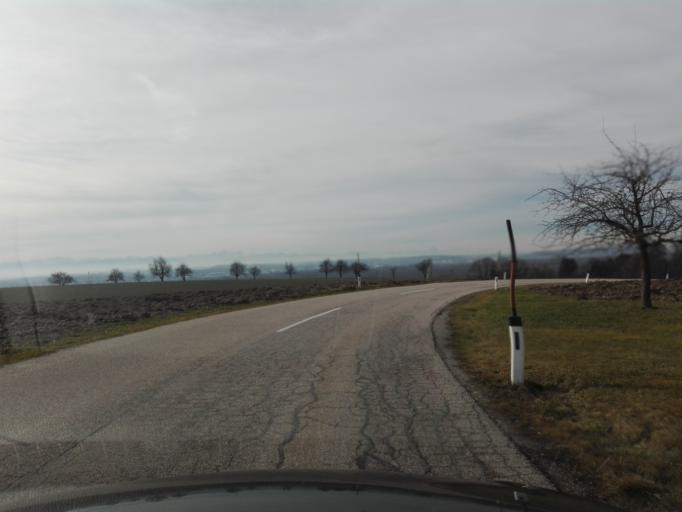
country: AT
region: Lower Austria
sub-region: Politischer Bezirk Amstetten
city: Ennsdorf
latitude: 48.2542
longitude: 14.4970
